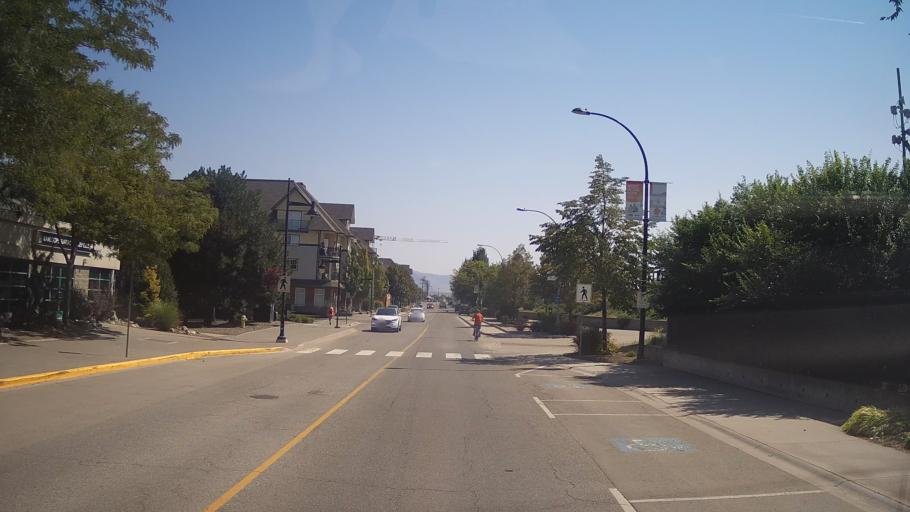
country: CA
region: British Columbia
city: Kamloops
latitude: 50.6781
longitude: -120.3328
